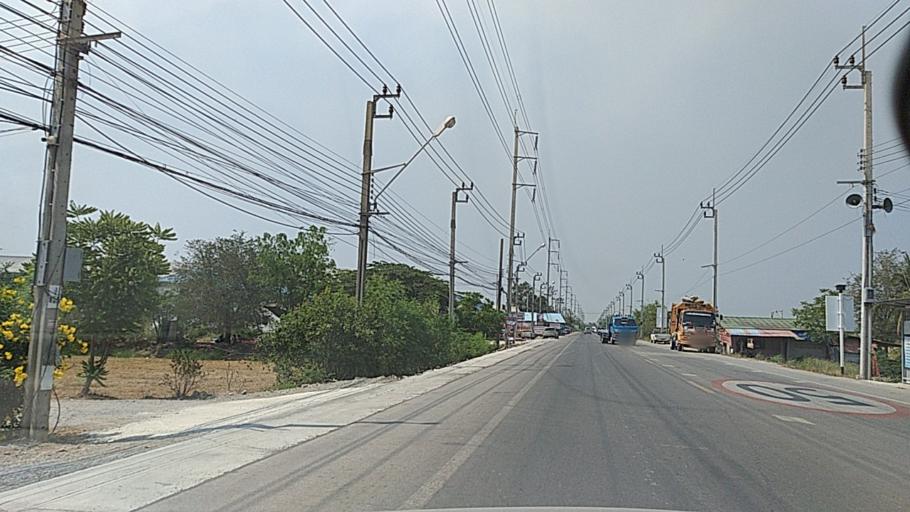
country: TH
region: Nonthaburi
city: Sai Noi
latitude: 13.9220
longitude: 100.3205
